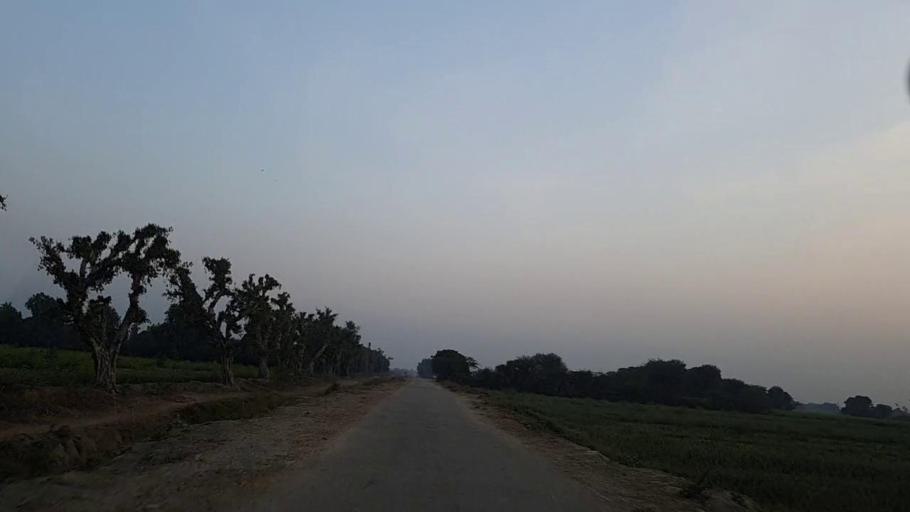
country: PK
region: Sindh
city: Tando Ghulam Ali
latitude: 25.1195
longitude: 68.8986
